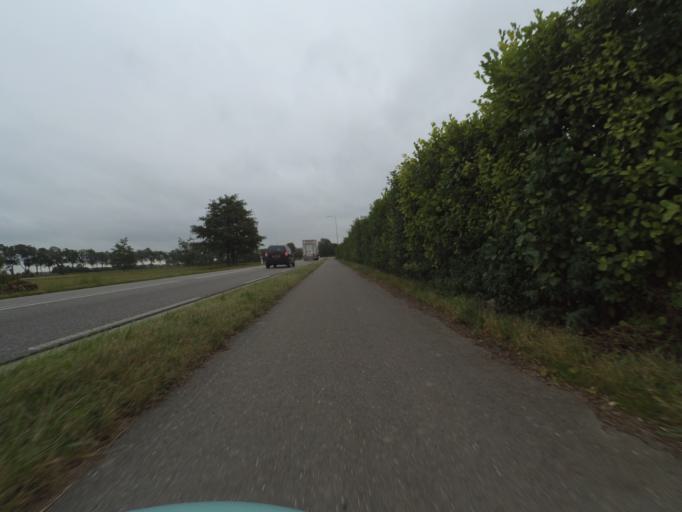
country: NL
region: Gelderland
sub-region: Gemeente Geldermalsen
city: Geldermalsen
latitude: 51.9094
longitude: 5.3449
